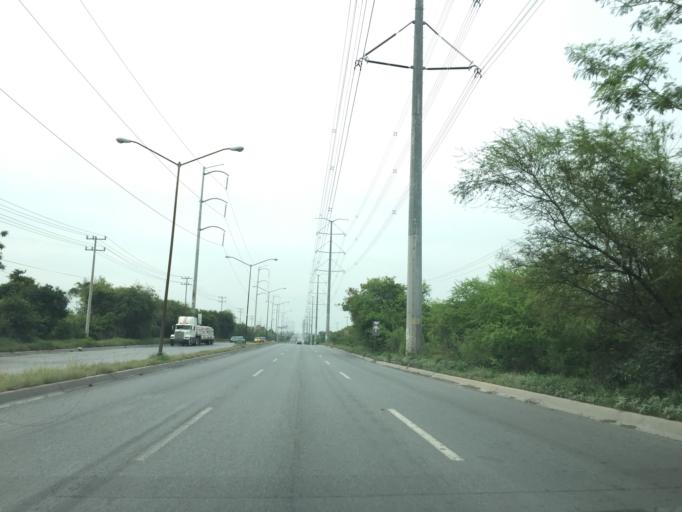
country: MX
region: Nuevo Leon
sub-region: Apodaca
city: Fraccionamiento Cosmopolis Octavo Sector
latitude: 25.7890
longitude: -100.2233
